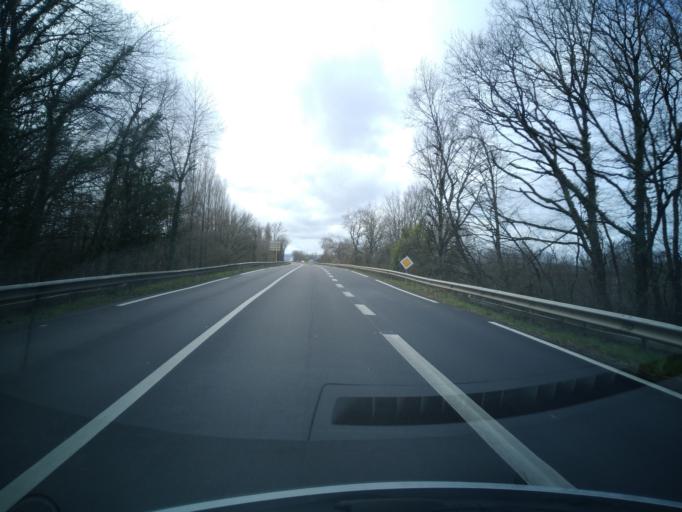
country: FR
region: Bourgogne
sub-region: Departement de Saone-et-Loire
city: Montchanin
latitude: 46.7576
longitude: 4.4741
